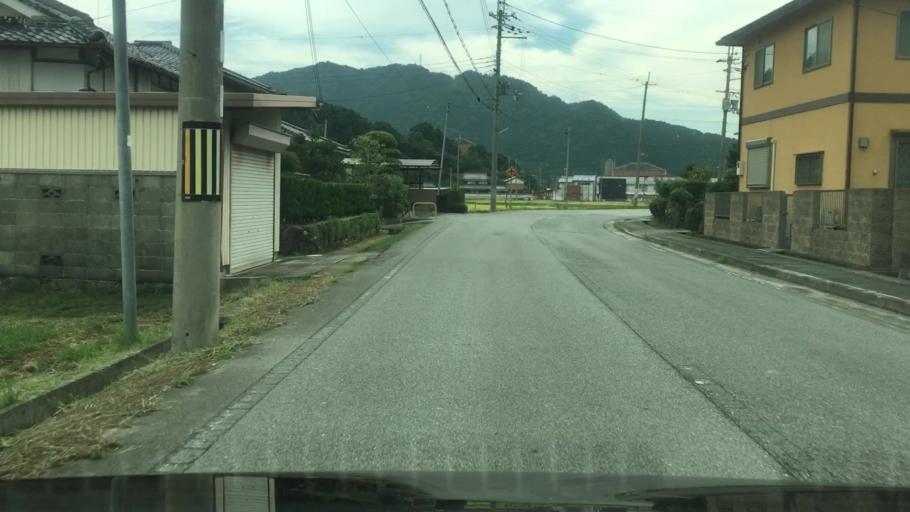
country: JP
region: Hyogo
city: Sasayama
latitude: 35.0702
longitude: 135.1843
